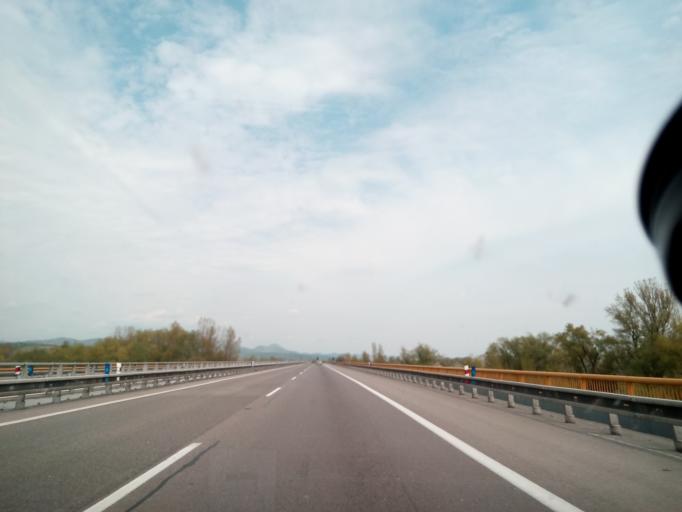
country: SK
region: Nitriansky
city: Nemsova
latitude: 48.9313
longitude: 18.0865
